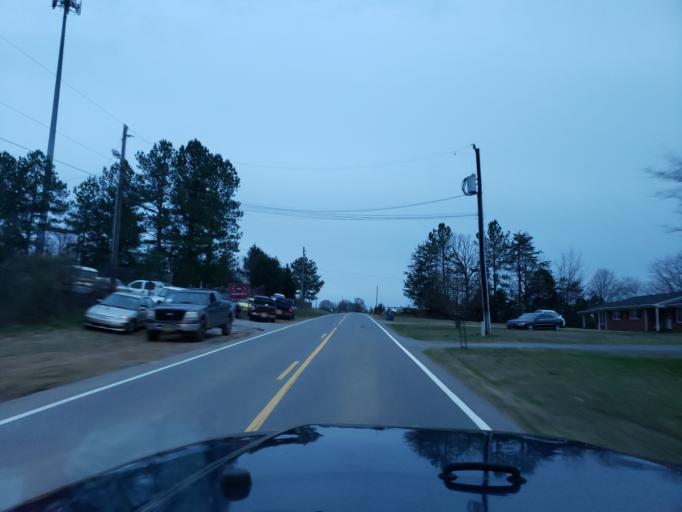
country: US
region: North Carolina
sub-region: Cleveland County
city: White Plains
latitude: 35.2176
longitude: -81.4560
